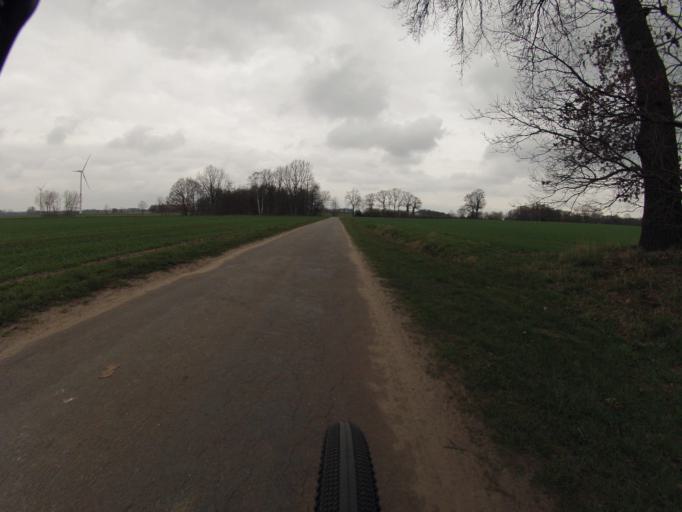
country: DE
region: North Rhine-Westphalia
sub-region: Regierungsbezirk Munster
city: Mettingen
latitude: 52.3403
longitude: 7.8127
